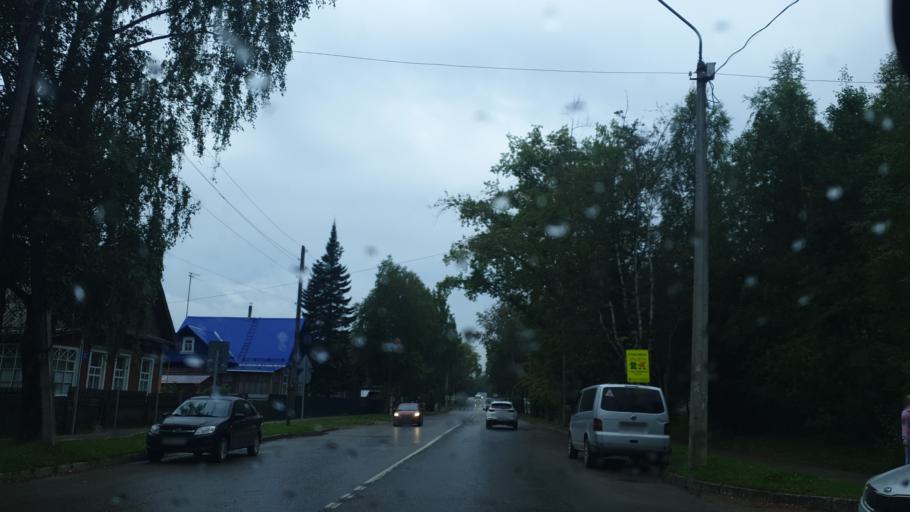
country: RU
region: Komi Republic
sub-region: Syktyvdinskiy Rayon
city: Syktyvkar
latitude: 61.6589
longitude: 50.8283
